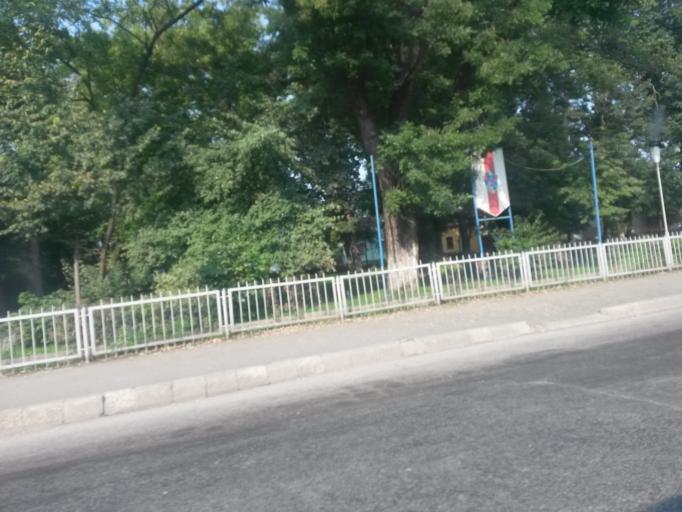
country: RO
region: Cluj
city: Turda
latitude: 46.5792
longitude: 23.7727
